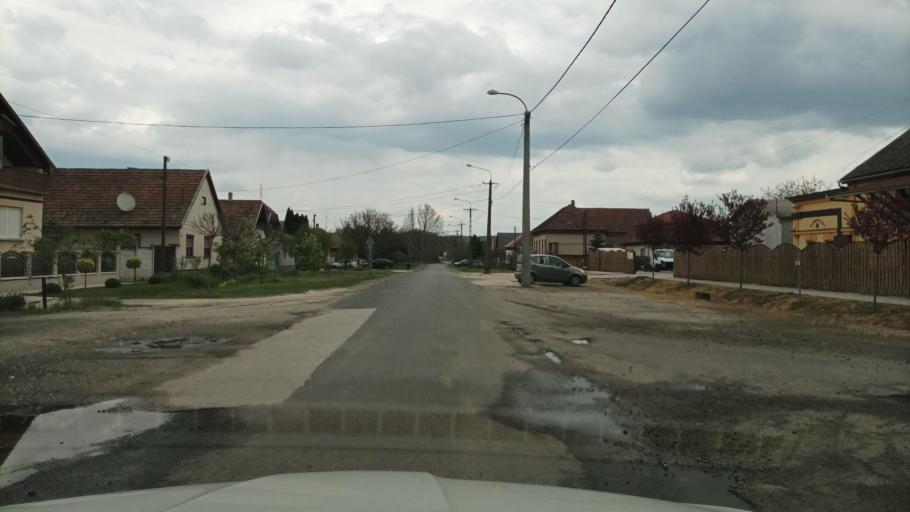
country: HU
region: Pest
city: Cegledbercel
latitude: 47.2175
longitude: 19.6590
